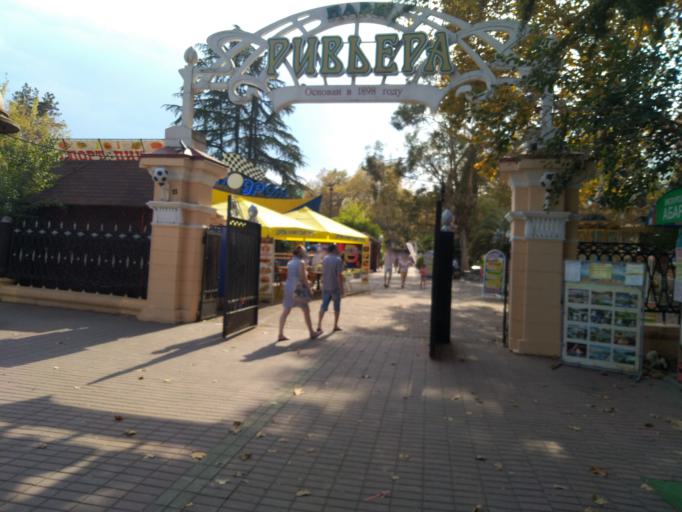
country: RU
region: Krasnodarskiy
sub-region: Sochi City
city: Sochi
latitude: 43.5935
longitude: 39.7174
